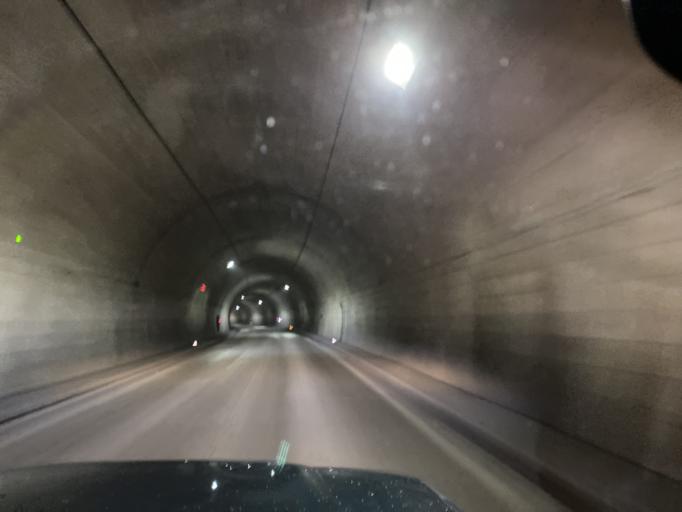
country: JP
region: Toyama
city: Fukumitsu
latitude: 36.3096
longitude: 136.8922
